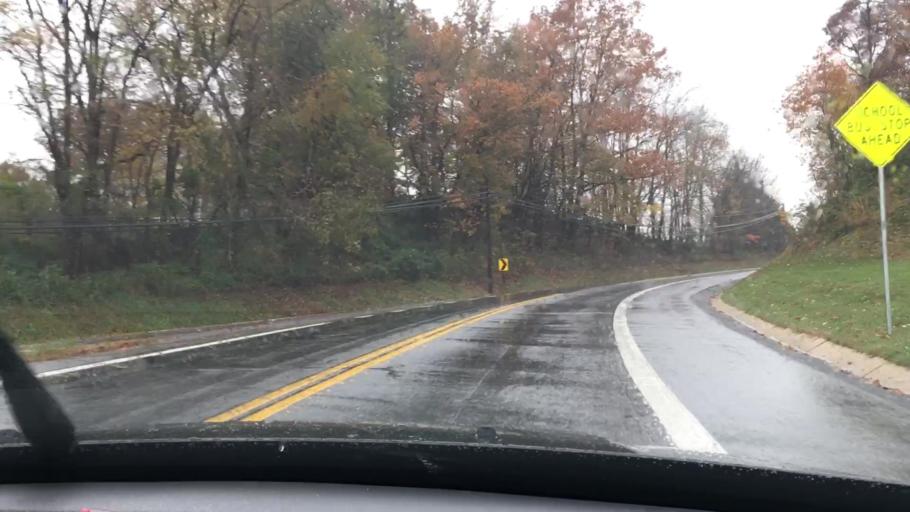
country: US
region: Maryland
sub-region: Frederick County
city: Urbana
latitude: 39.3219
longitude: -77.3620
